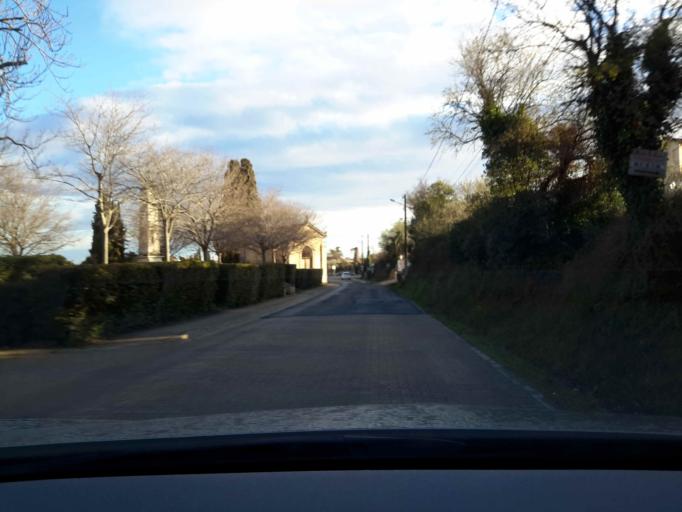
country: FR
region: Languedoc-Roussillon
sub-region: Departement du Gard
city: Beauvoisin
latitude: 43.7228
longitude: 4.3265
